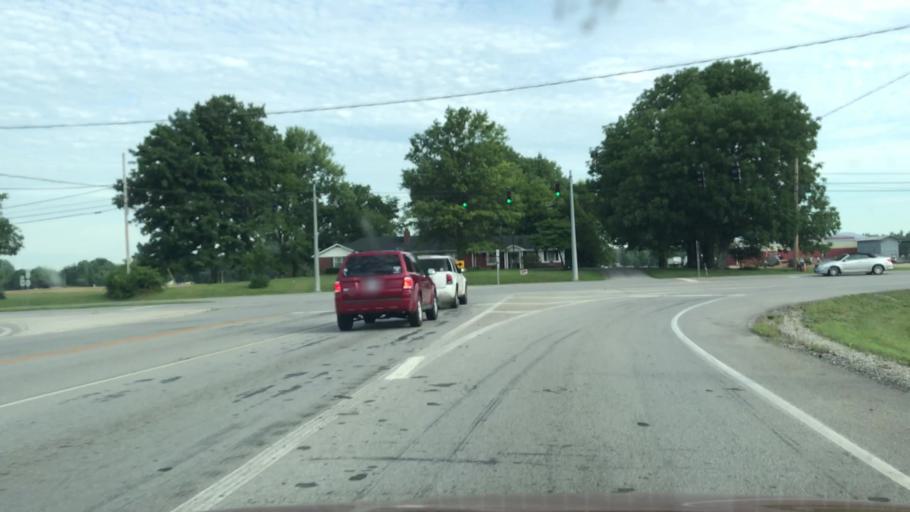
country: US
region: Kentucky
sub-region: Warren County
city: Bowling Green
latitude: 37.0384
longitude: -86.3333
